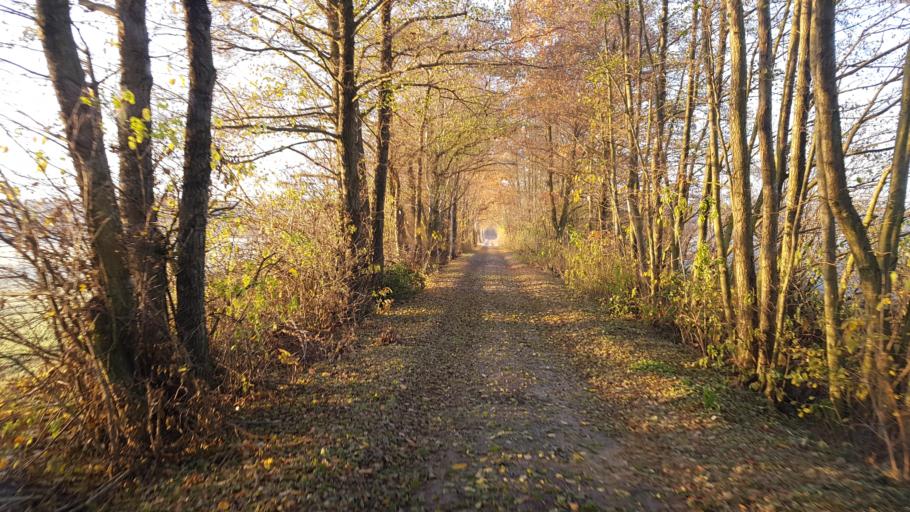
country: DE
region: Brandenburg
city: Sallgast
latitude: 51.6079
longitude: 13.8396
